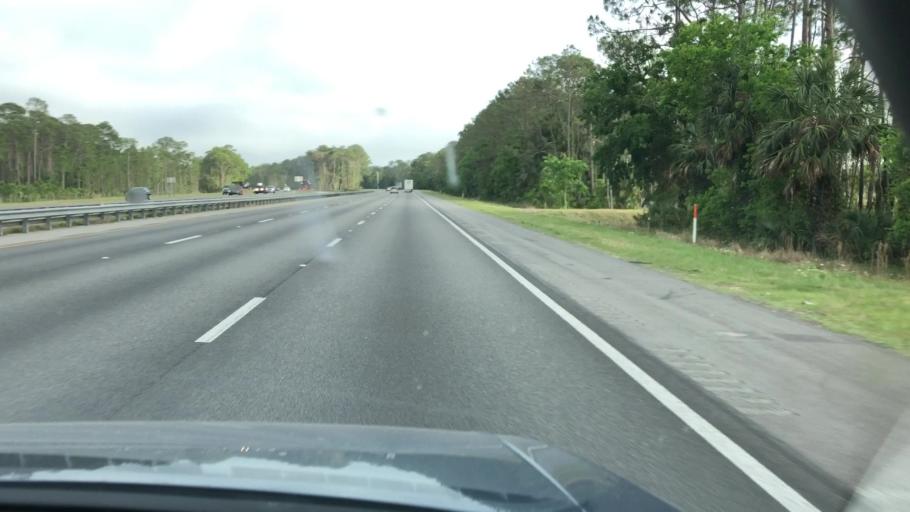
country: US
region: Florida
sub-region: Volusia County
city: South Daytona
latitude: 29.1357
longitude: -81.0646
